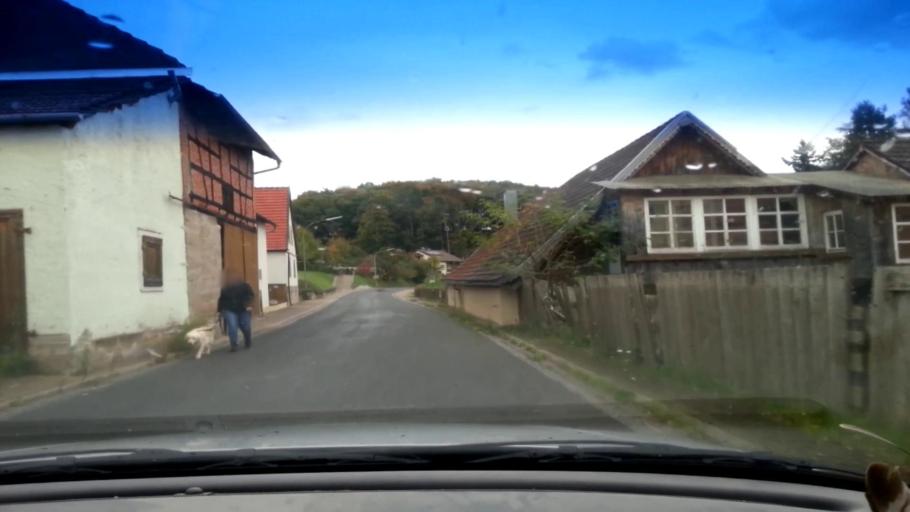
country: DE
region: Bavaria
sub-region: Regierungsbezirk Unterfranken
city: Stettfeld
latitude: 49.9993
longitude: 10.7464
